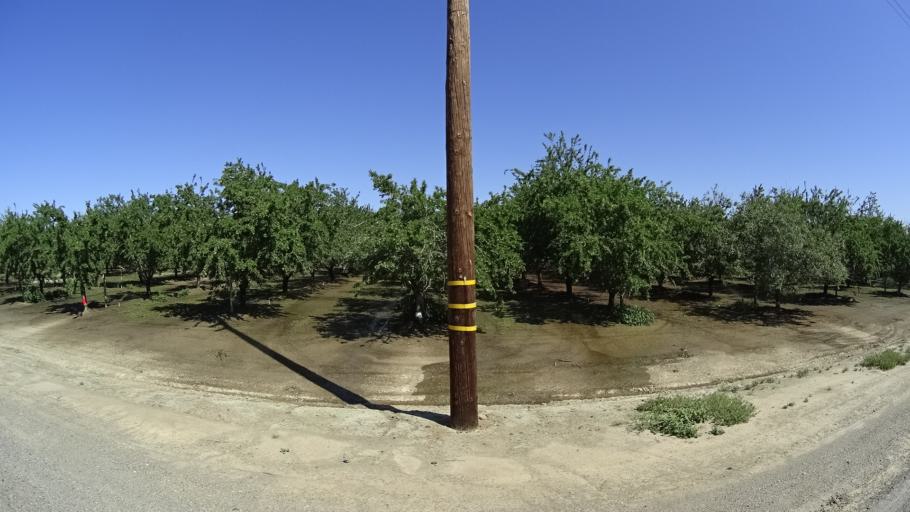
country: US
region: California
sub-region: Glenn County
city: Orland
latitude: 39.7108
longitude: -122.1562
